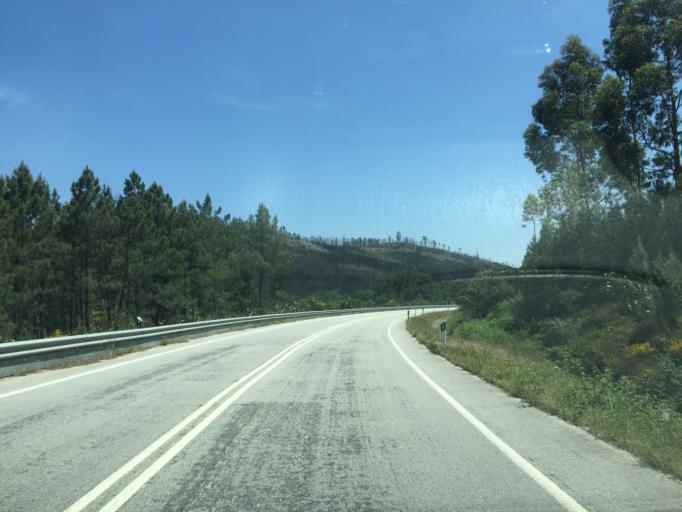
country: PT
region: Castelo Branco
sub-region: Vila de Rei
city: Vila de Rei
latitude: 39.6682
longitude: -8.1325
